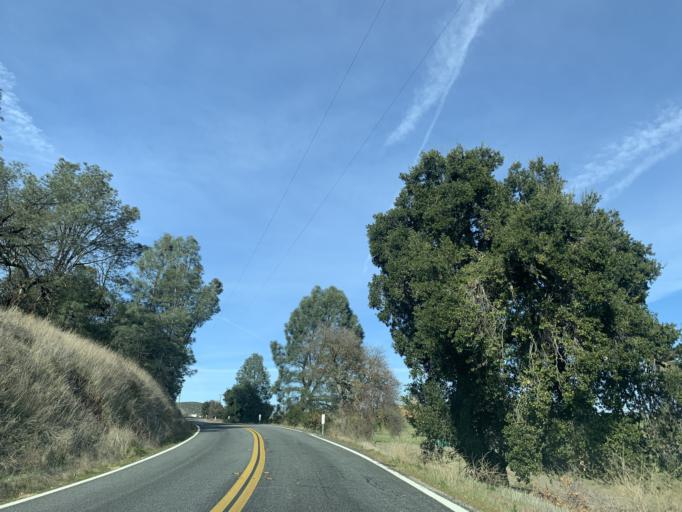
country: US
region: California
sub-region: Monterey County
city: Soledad
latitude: 36.5584
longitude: -121.1712
